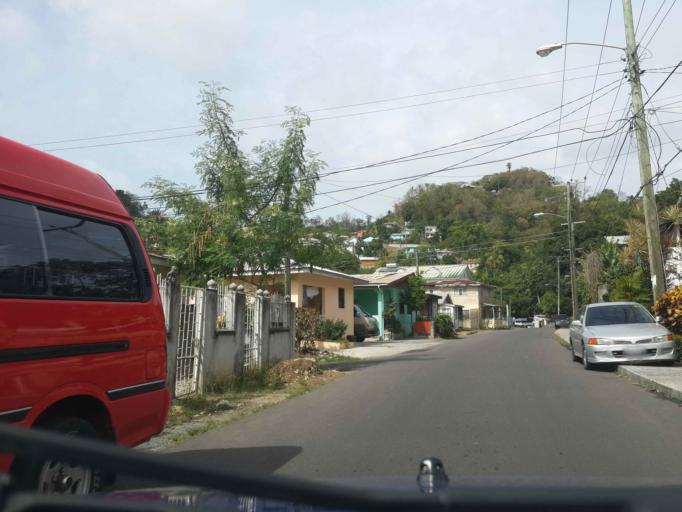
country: LC
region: Castries Quarter
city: Bisee
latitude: 14.0185
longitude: -60.9817
